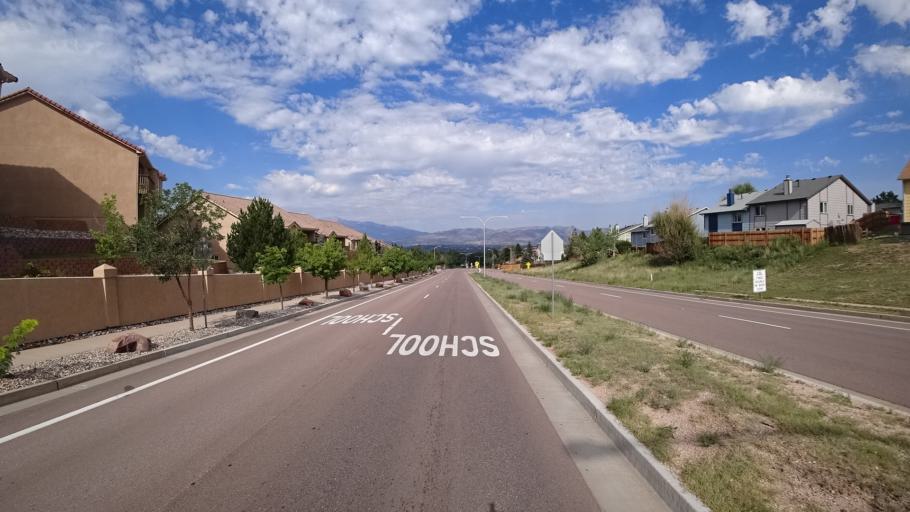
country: US
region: Colorado
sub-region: El Paso County
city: Cimarron Hills
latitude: 38.8953
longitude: -104.7290
